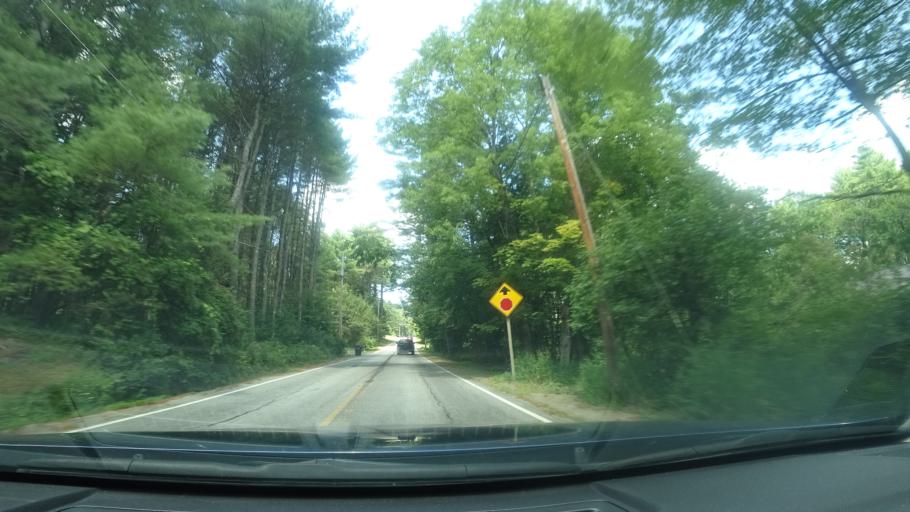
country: US
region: New York
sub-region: Warren County
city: Warrensburg
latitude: 43.6609
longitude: -73.8347
